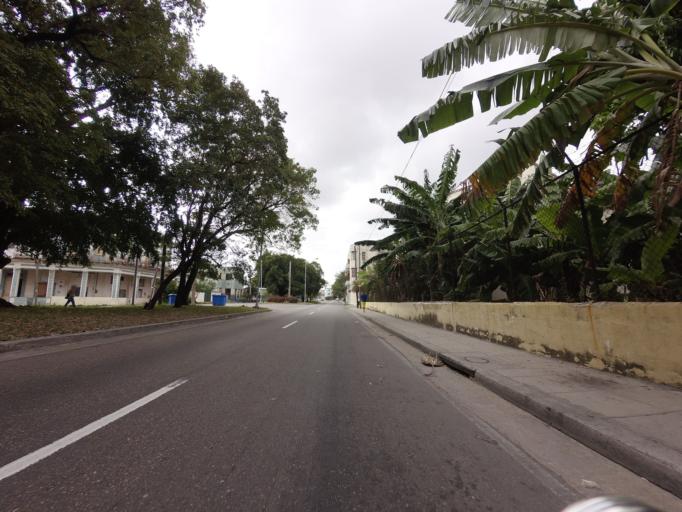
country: CU
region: La Habana
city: Havana
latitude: 23.1292
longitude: -82.3901
